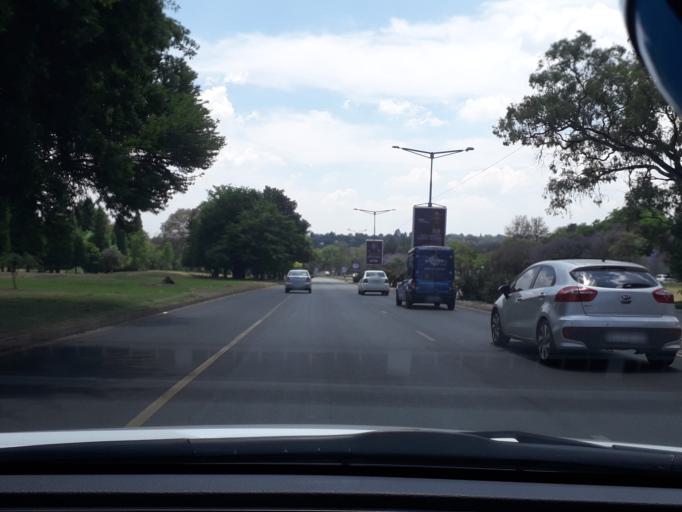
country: ZA
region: Gauteng
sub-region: City of Johannesburg Metropolitan Municipality
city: Johannesburg
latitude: -26.1063
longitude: 28.0318
